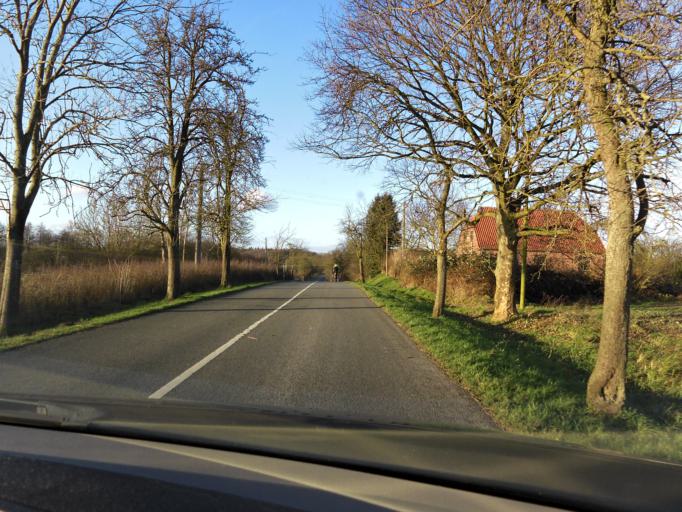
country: DE
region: Schleswig-Holstein
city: Kittlitz
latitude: 53.6612
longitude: 10.9669
